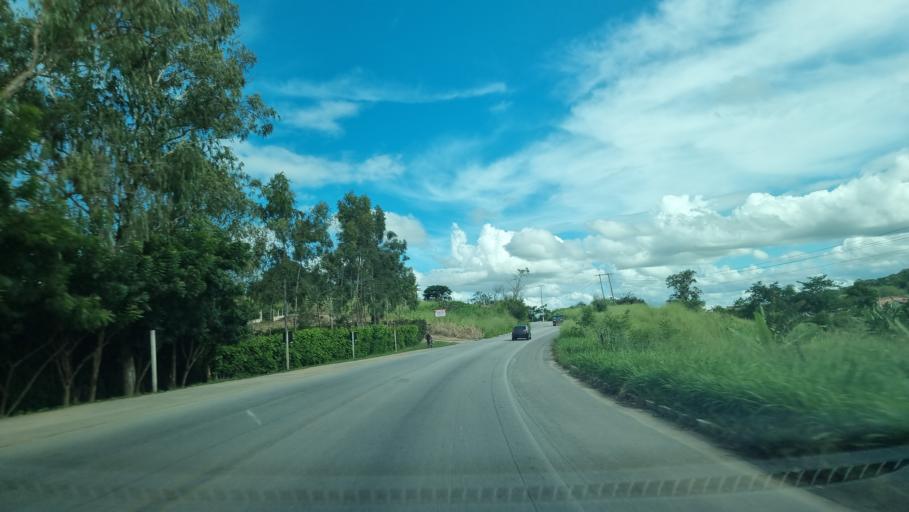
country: BR
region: Pernambuco
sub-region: Caruaru
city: Caruaru
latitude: -8.3718
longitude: -35.9836
